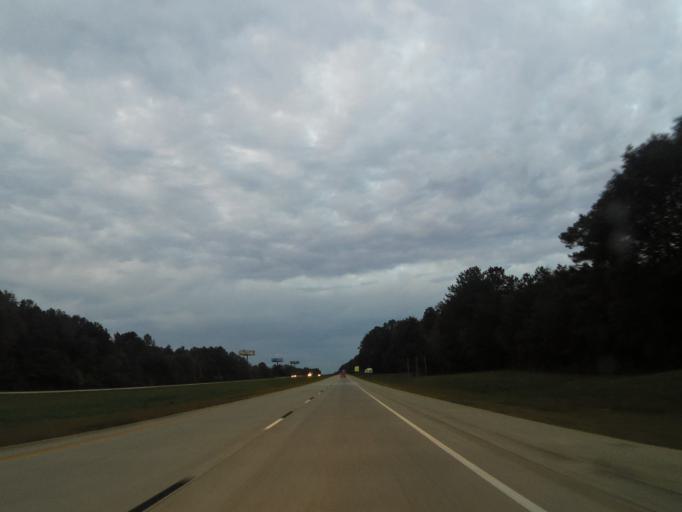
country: US
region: Alabama
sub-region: Etowah County
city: Gadsden
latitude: 34.0606
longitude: -86.0355
